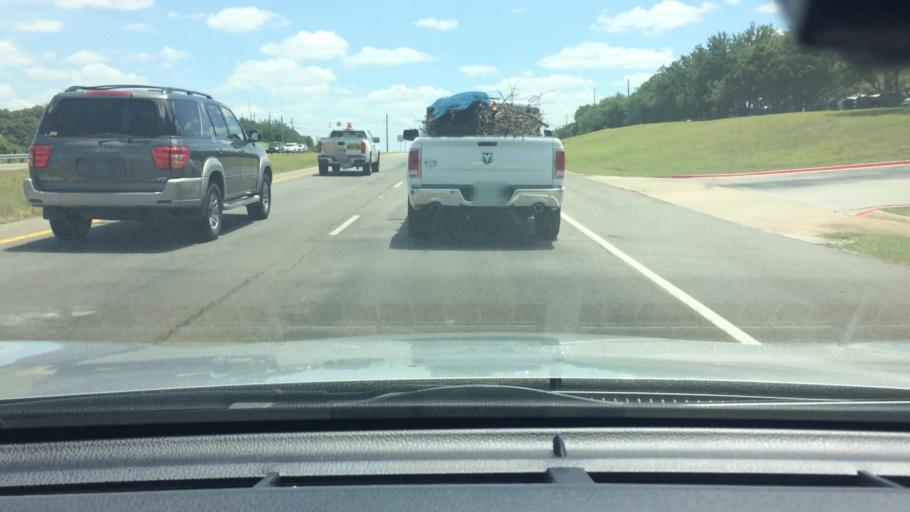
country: US
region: Texas
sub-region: Travis County
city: Lost Creek
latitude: 30.2812
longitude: -97.8225
